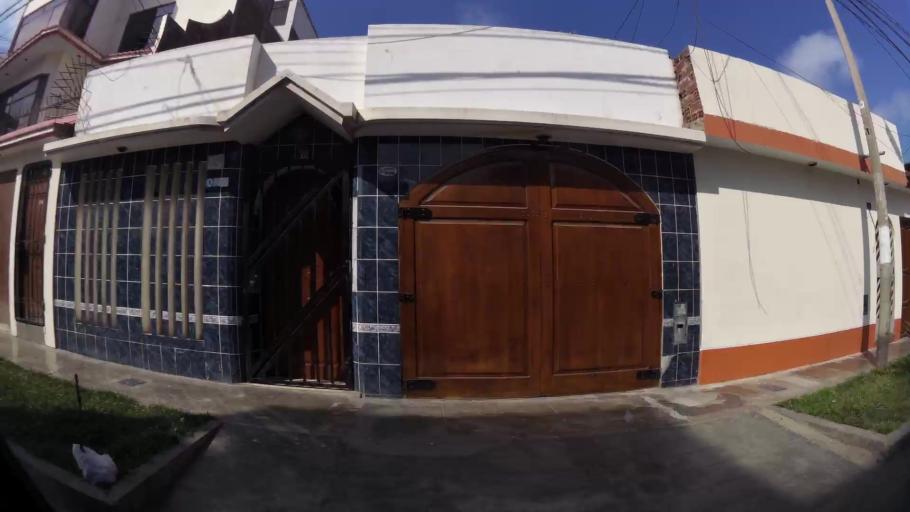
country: PE
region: La Libertad
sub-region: Provincia de Trujillo
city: Trujillo
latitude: -8.1229
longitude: -79.0189
